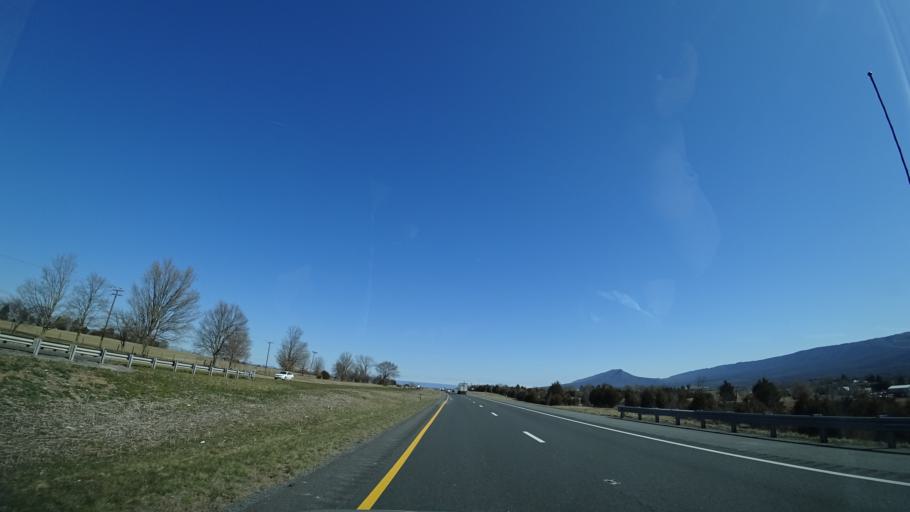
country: US
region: Virginia
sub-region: Shenandoah County
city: New Market
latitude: 38.6634
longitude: -78.6663
